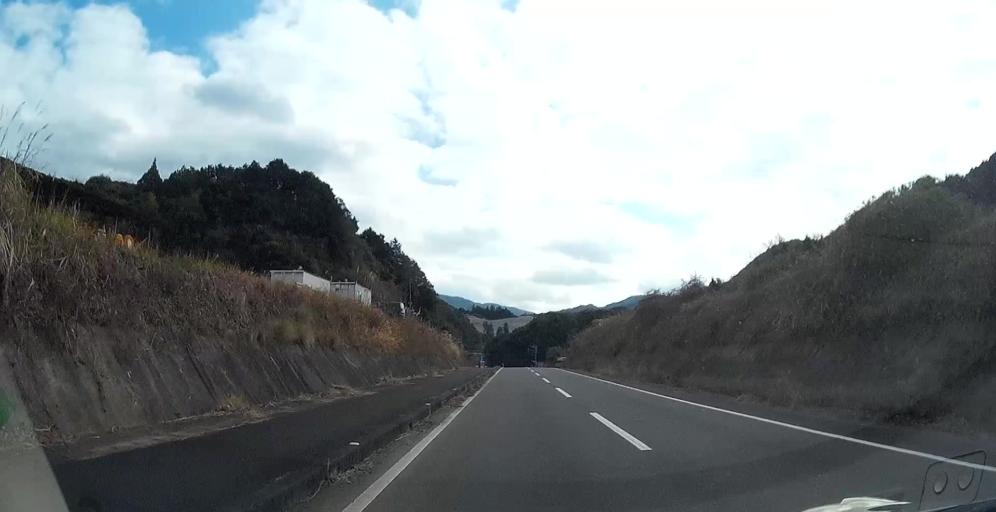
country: JP
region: Kumamoto
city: Minamata
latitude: 32.2290
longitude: 130.4312
